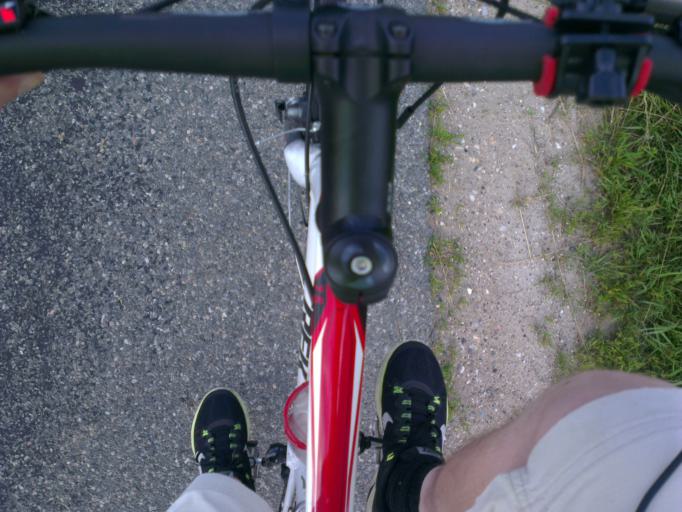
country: DK
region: Capital Region
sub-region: Frederikssund Kommune
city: Skibby
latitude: 55.7456
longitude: 12.0179
